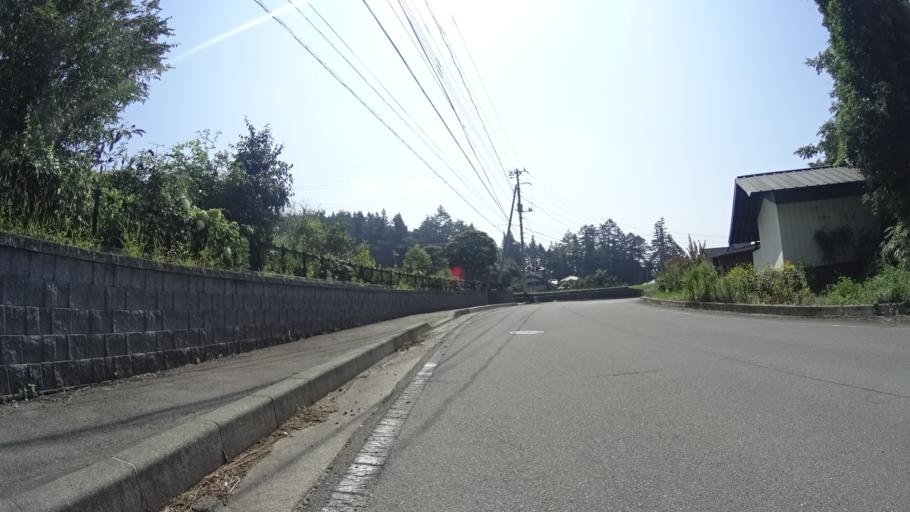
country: JP
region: Nagano
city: Chino
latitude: 35.8645
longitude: 138.3034
